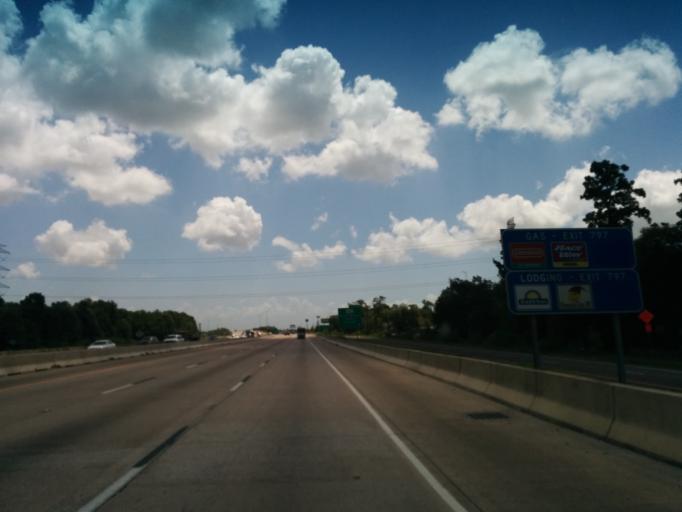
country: US
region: Texas
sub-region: Chambers County
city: Mont Belvieu
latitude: 29.8210
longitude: -94.9089
